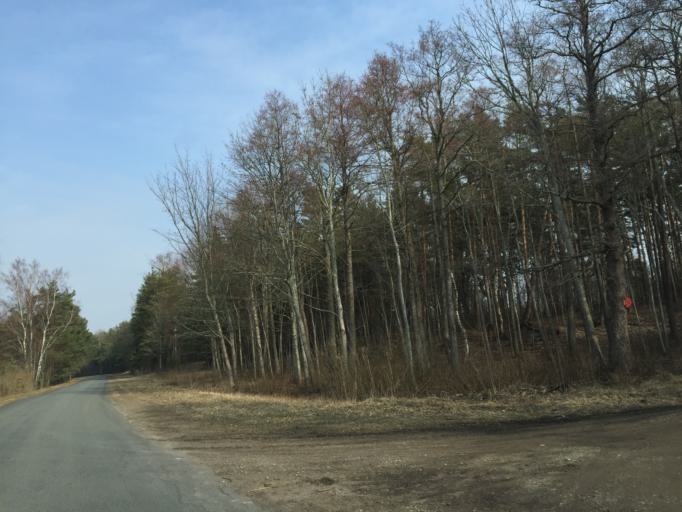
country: LV
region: Salacgrivas
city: Ainazi
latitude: 57.8807
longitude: 24.3642
